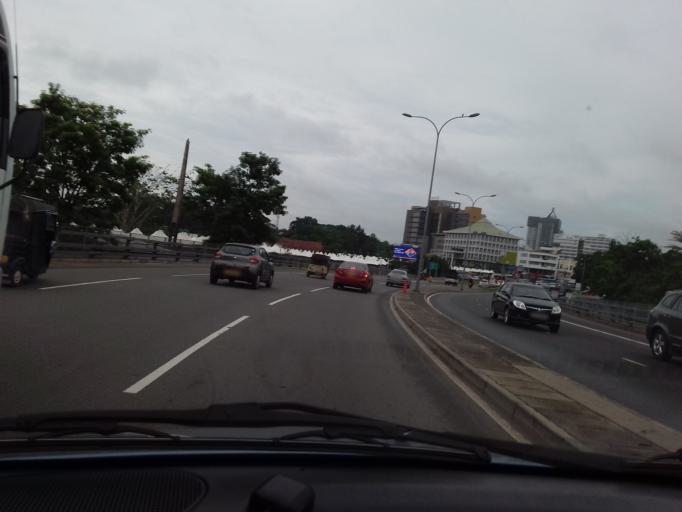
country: LK
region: Western
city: Battaramulla South
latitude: 6.9034
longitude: 79.9091
